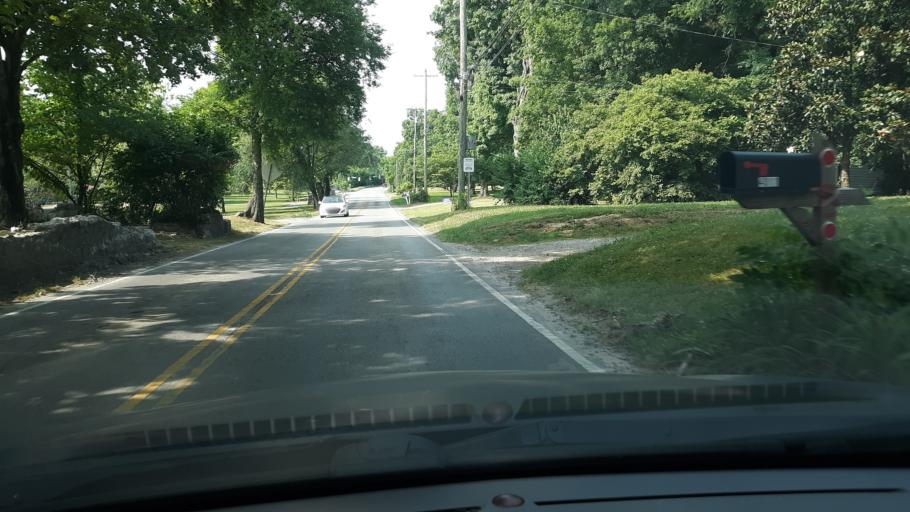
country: US
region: Tennessee
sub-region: Davidson County
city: Lakewood
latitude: 36.1755
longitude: -86.6142
